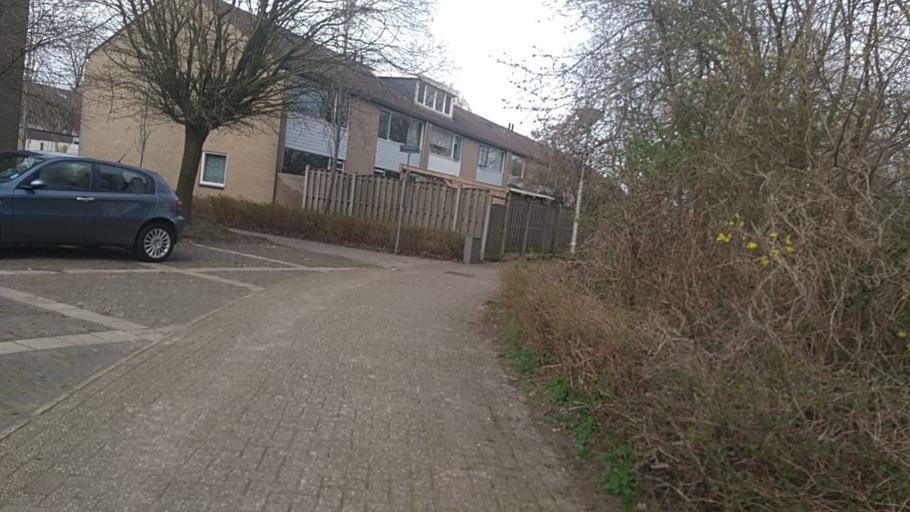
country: NL
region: Overijssel
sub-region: Gemeente Almelo
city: Almelo
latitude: 52.3765
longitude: 6.6737
